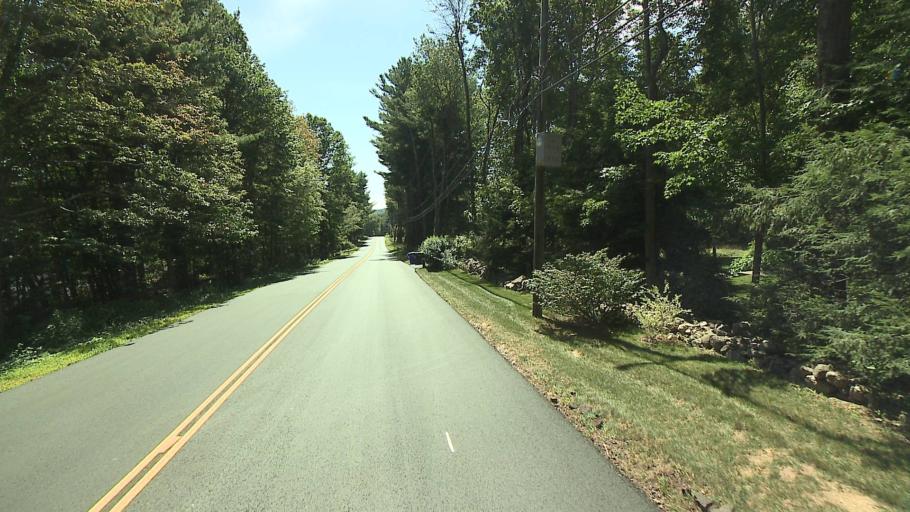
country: US
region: Connecticut
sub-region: Hartford County
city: West Simsbury
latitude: 41.9154
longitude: -72.9024
